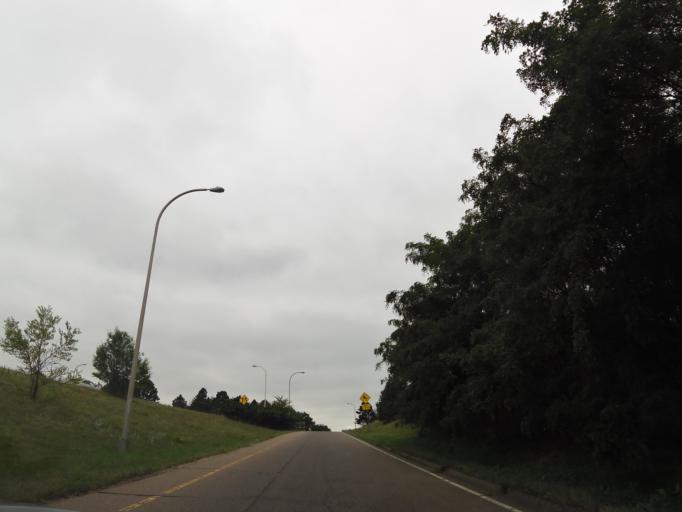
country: US
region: Colorado
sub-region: El Paso County
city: Colorado Springs
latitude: 38.7957
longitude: -104.8228
